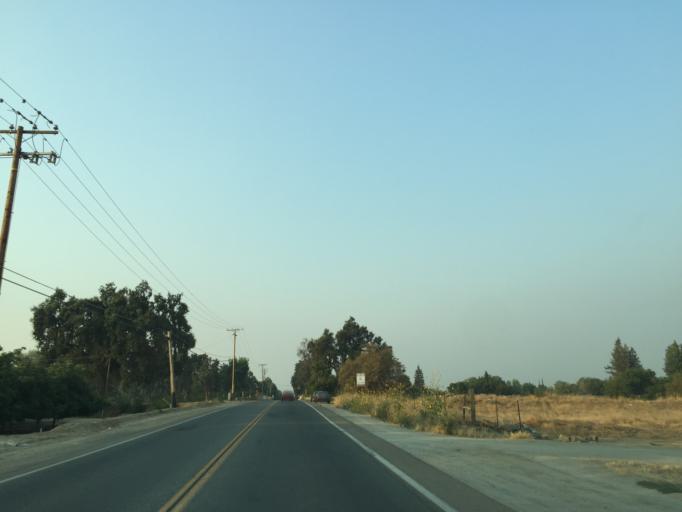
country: US
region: California
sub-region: Tulare County
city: Visalia
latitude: 36.3550
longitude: -119.2790
